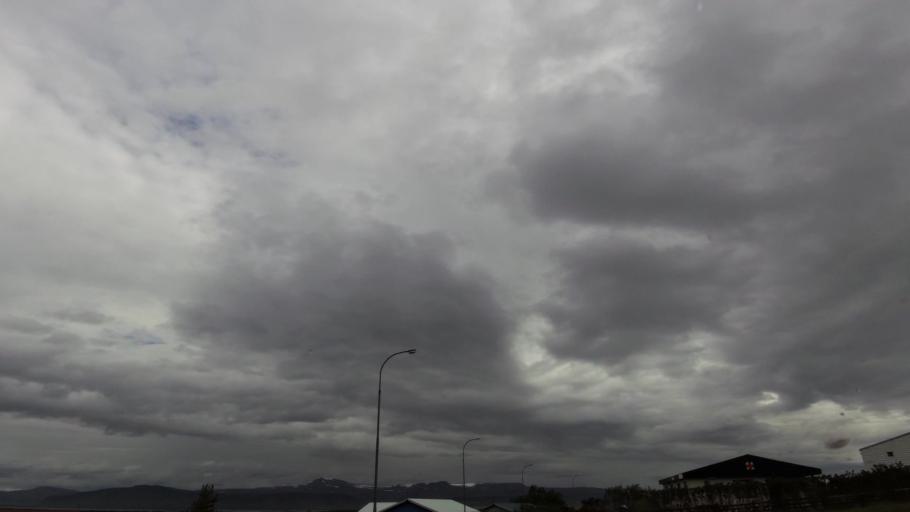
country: IS
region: West
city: Stykkisholmur
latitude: 65.4492
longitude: -22.2011
